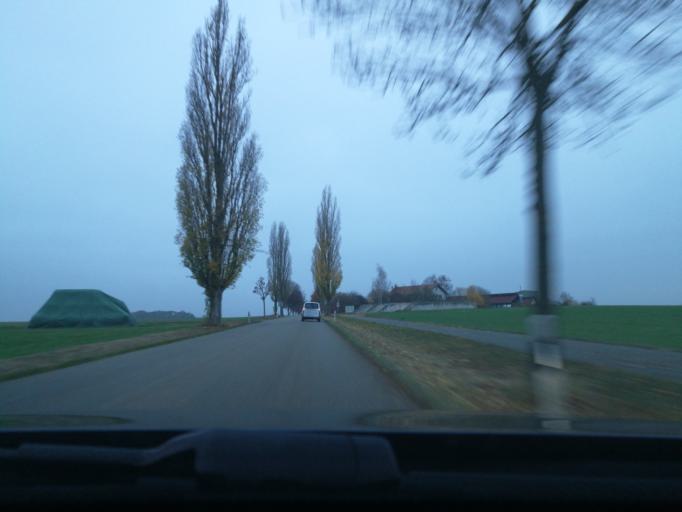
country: DE
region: Bavaria
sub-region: Regierungsbezirk Mittelfranken
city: Obermichelbach
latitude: 49.5169
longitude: 10.9216
